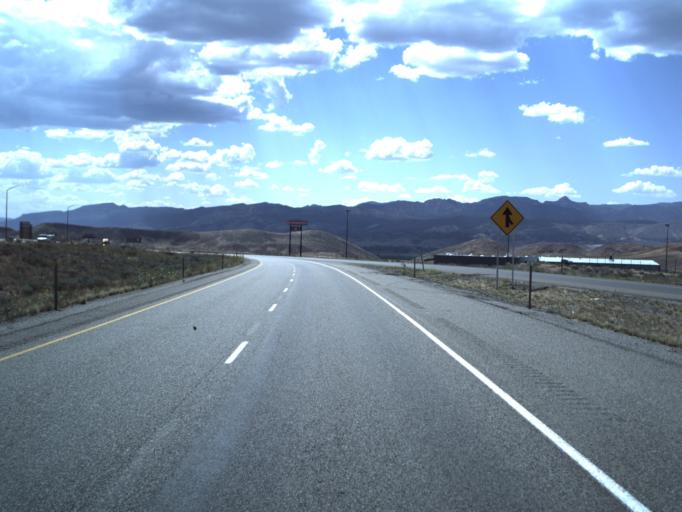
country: US
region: Utah
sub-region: Sevier County
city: Salina
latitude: 38.9335
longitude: -111.8593
